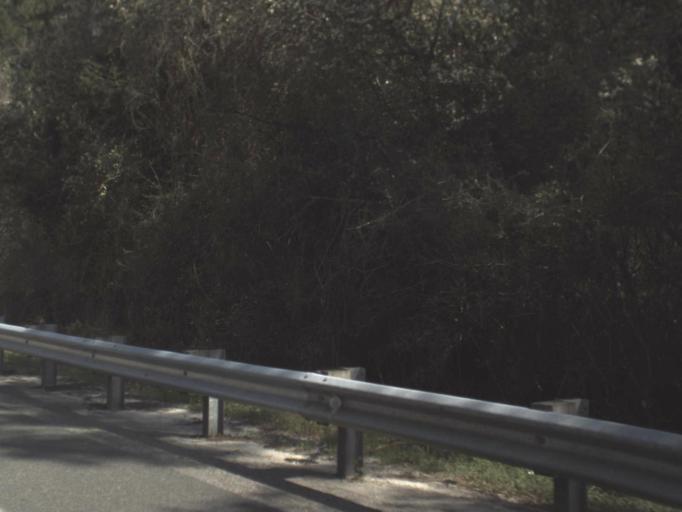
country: US
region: Florida
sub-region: Wakulla County
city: Crawfordville
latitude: 30.0765
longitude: -84.4230
